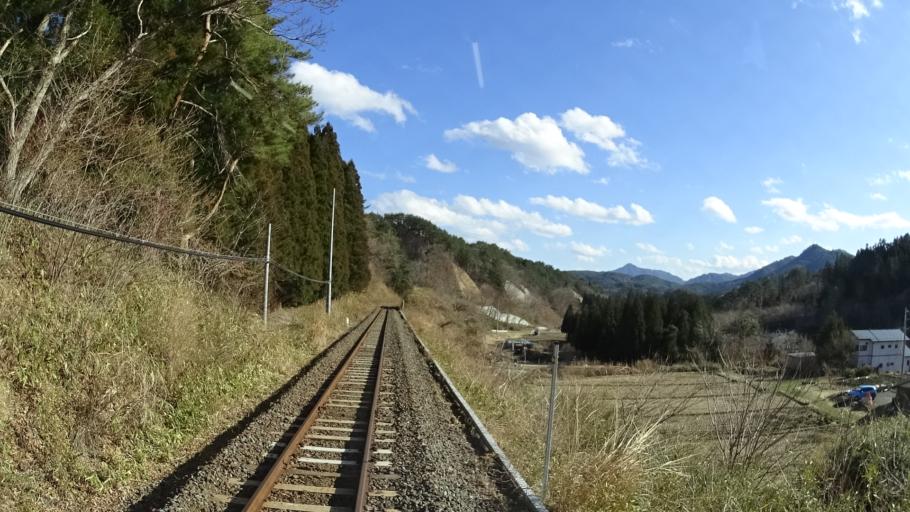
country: JP
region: Iwate
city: Yamada
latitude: 39.4884
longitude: 141.9241
